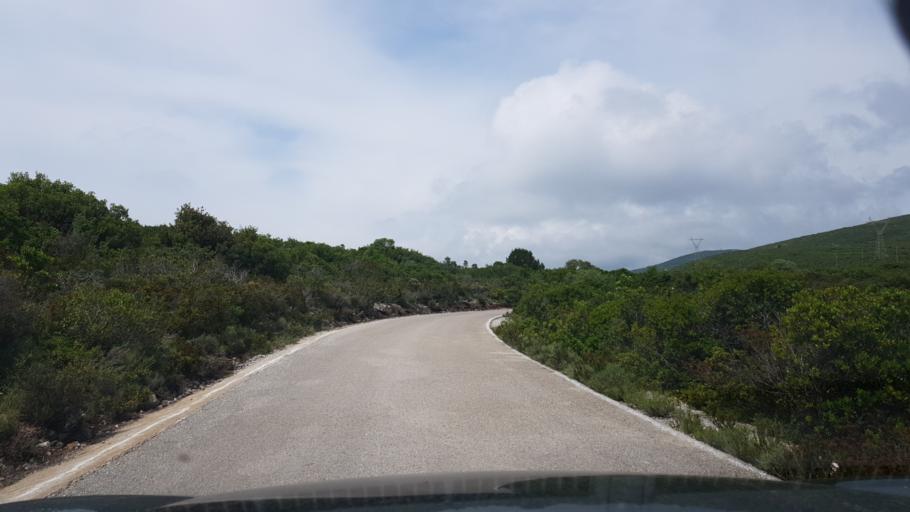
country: GR
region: Ionian Islands
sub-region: Lefkada
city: Nidri
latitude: 38.5976
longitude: 20.5561
